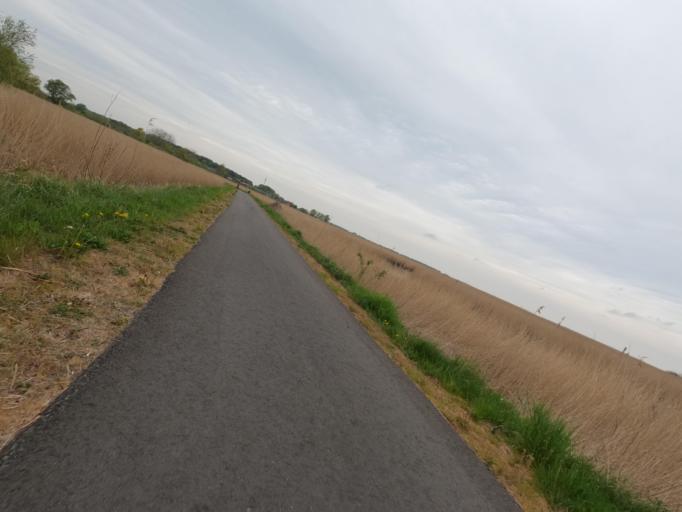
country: DE
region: Mecklenburg-Vorpommern
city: Ostseebad Dierhagen
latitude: 54.2513
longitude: 12.3957
